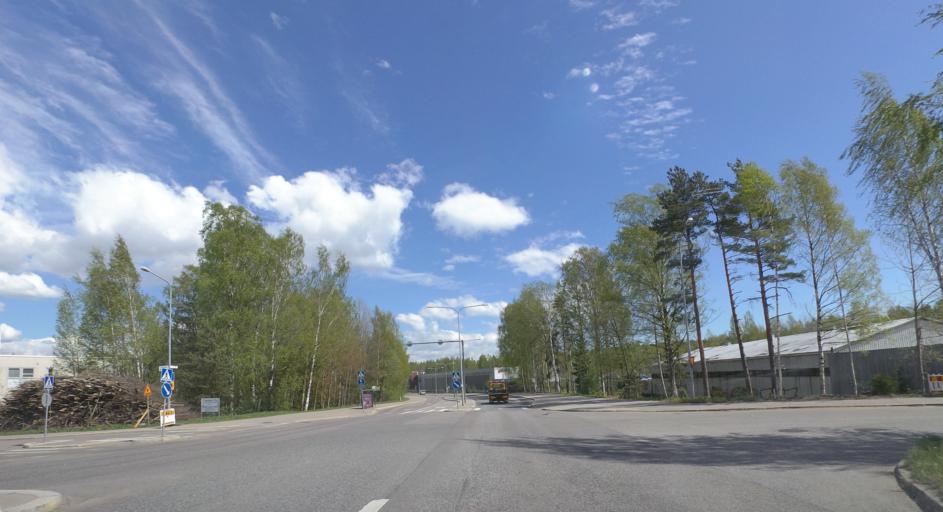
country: FI
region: Uusimaa
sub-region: Helsinki
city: Vantaa
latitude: 60.2473
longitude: 25.0547
